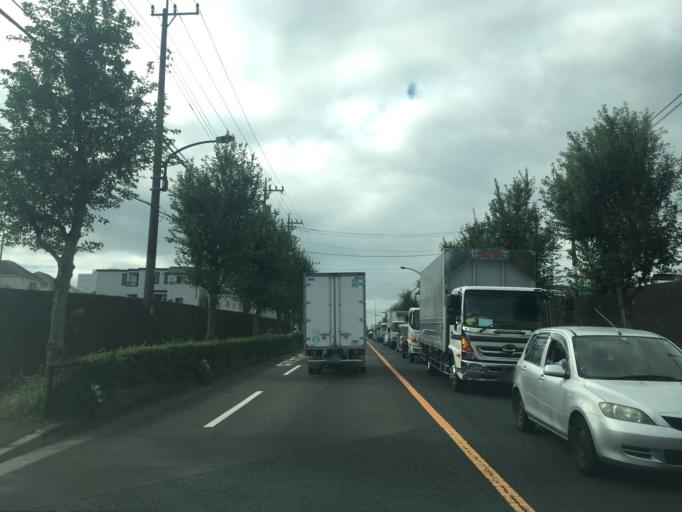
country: JP
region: Tokyo
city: Hino
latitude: 35.6769
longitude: 139.3651
